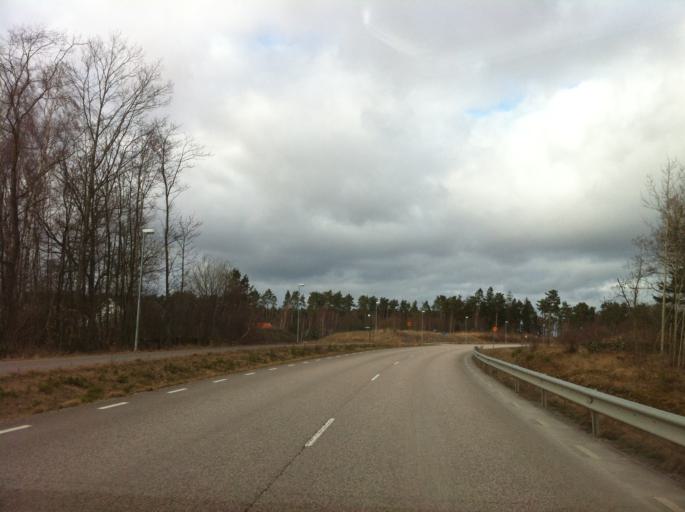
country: SE
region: Blekinge
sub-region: Solvesborgs Kommun
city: Soelvesborg
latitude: 56.0468
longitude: 14.6089
